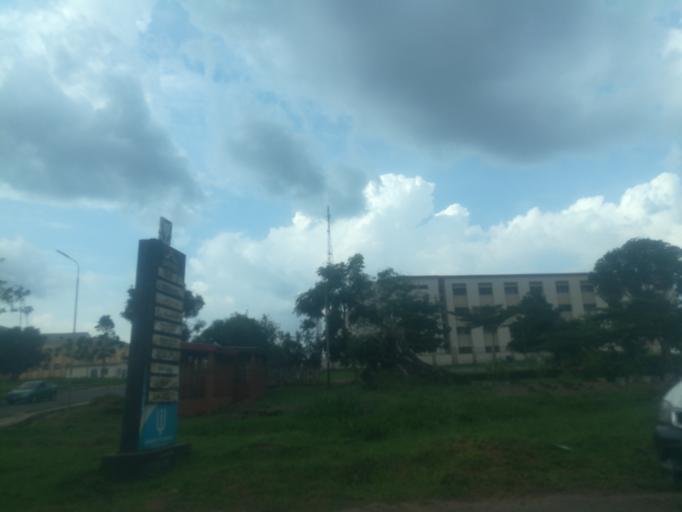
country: NG
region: Oyo
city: Ibadan
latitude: 7.4381
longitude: 3.8944
